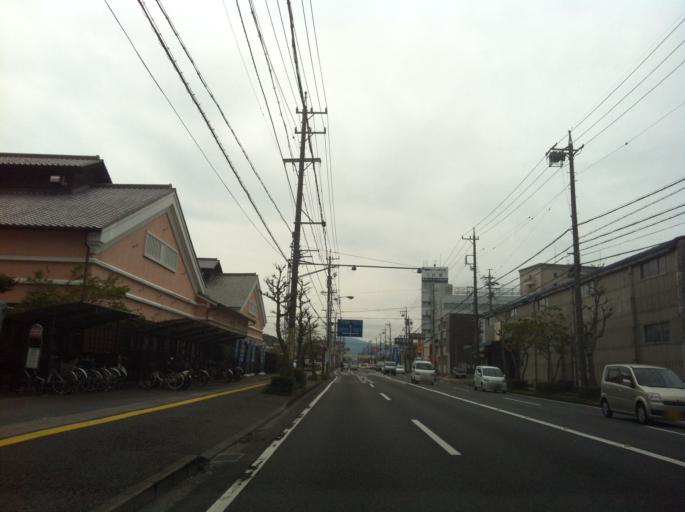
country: JP
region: Shizuoka
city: Shizuoka-shi
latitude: 34.9796
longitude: 138.4110
